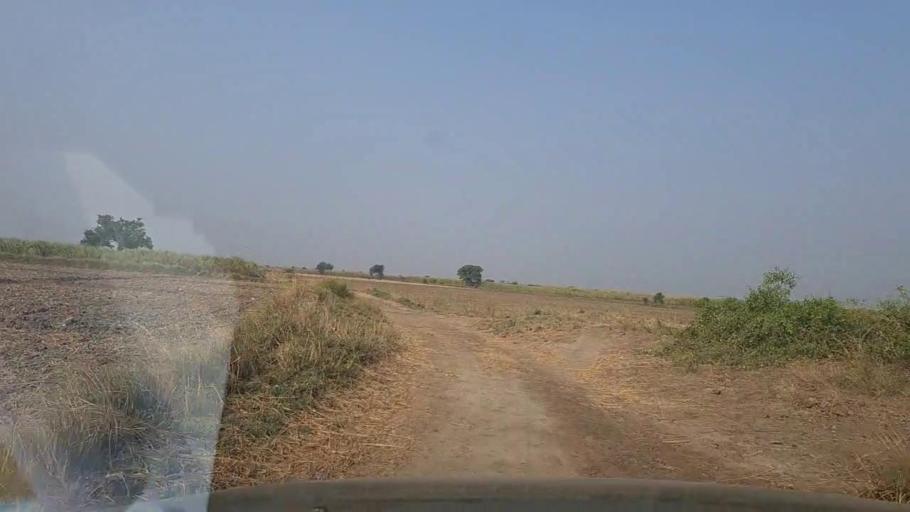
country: PK
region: Sindh
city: Bulri
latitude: 24.9409
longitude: 68.2778
